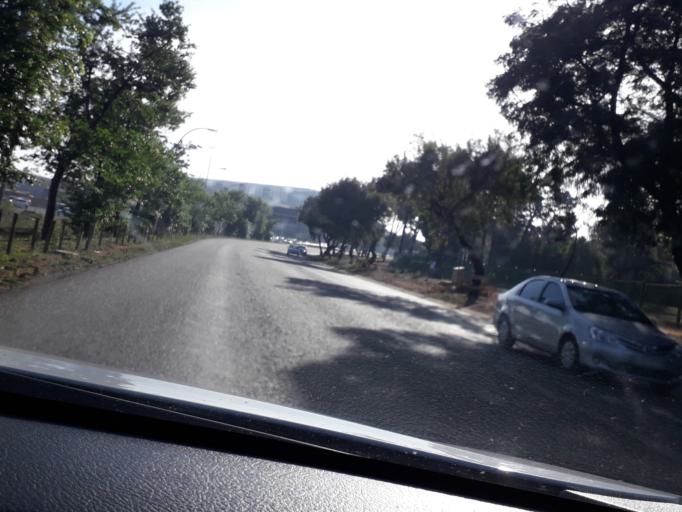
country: ZA
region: Gauteng
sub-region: Ekurhuleni Metropolitan Municipality
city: Germiston
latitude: -26.1649
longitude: 28.1733
